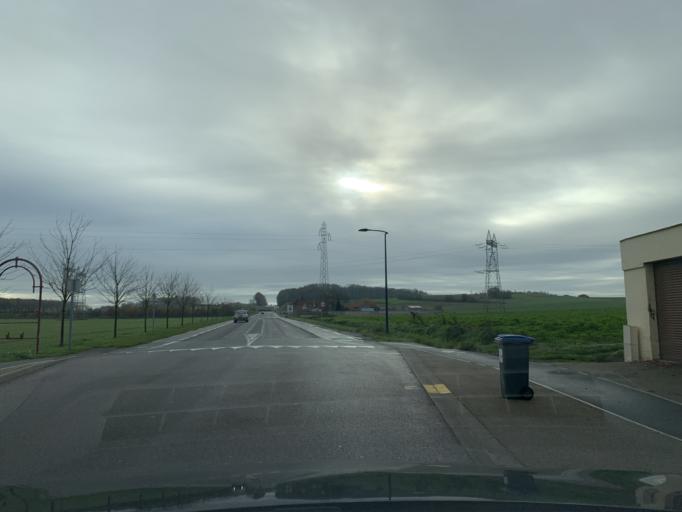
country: FR
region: Nord-Pas-de-Calais
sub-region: Departement du Nord
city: Cantin
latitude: 50.3078
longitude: 3.1297
